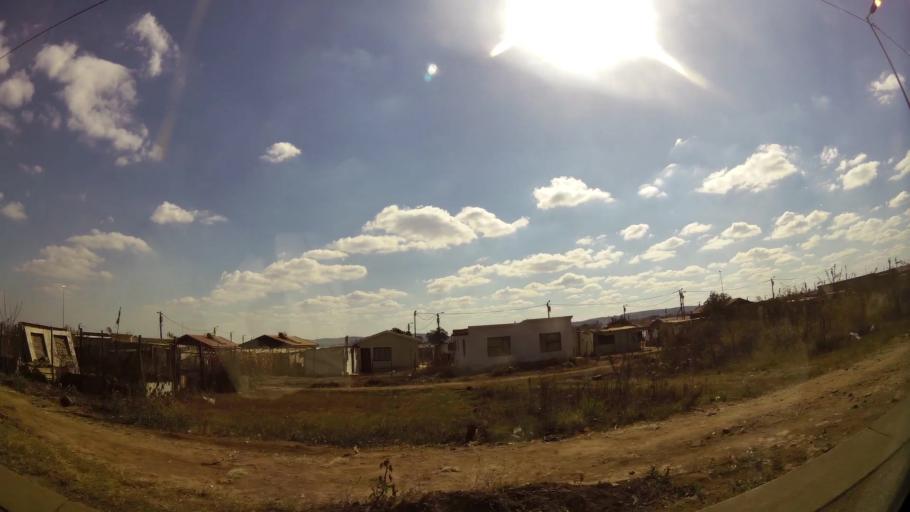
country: ZA
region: Gauteng
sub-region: City of Tshwane Metropolitan Municipality
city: Cullinan
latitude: -25.7345
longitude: 28.3960
